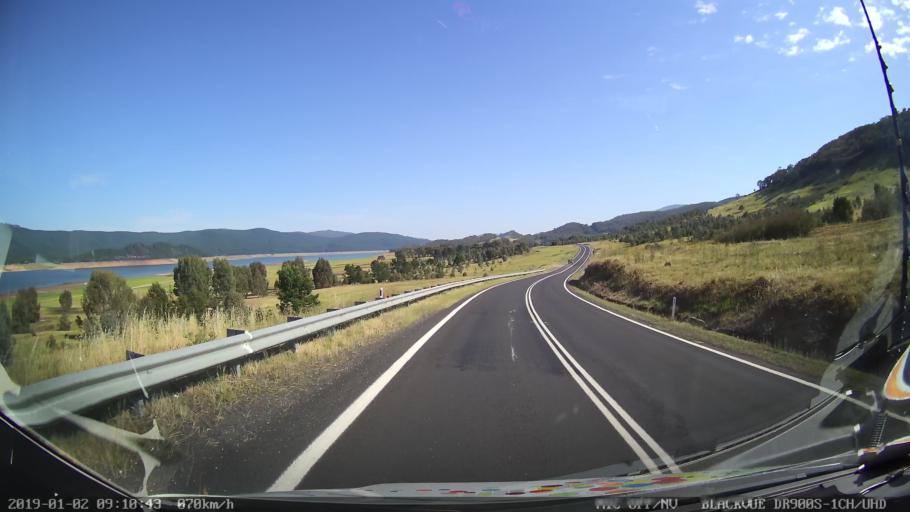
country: AU
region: New South Wales
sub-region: Tumut Shire
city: Tumut
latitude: -35.5190
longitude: 148.2683
